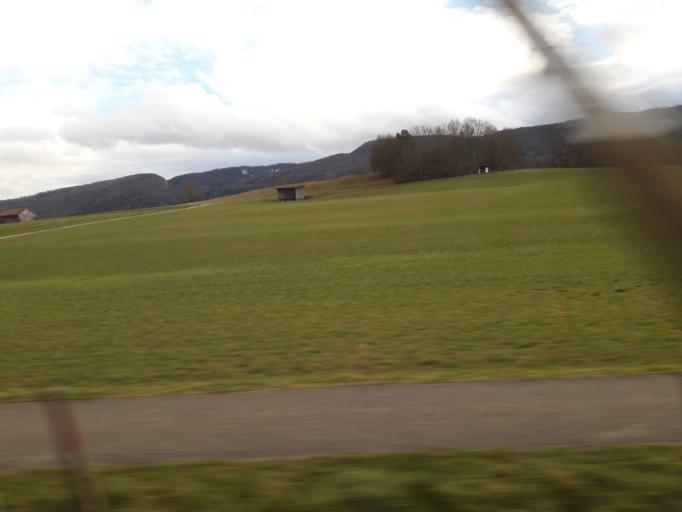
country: CH
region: Jura
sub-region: Delemont District
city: Courtetelle
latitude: 47.3391
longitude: 7.3090
